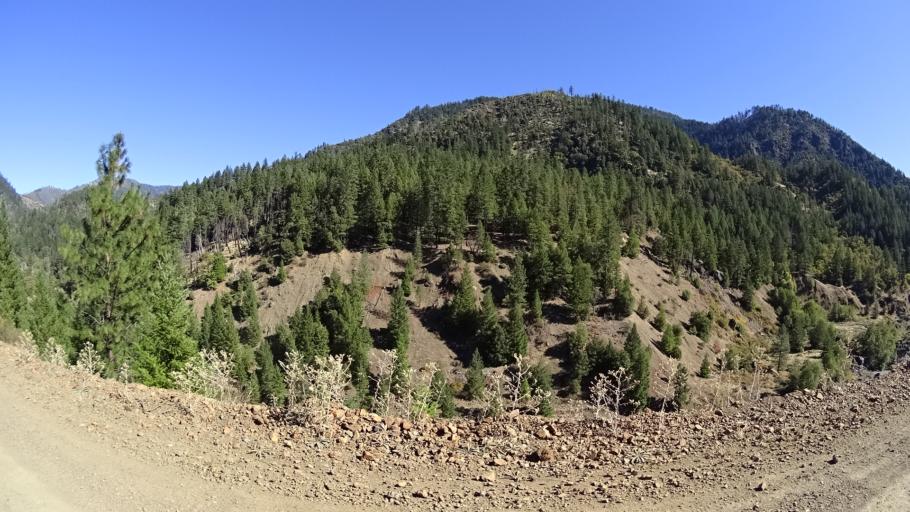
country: US
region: California
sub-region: Humboldt County
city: Willow Creek
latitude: 41.3111
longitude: -123.3772
